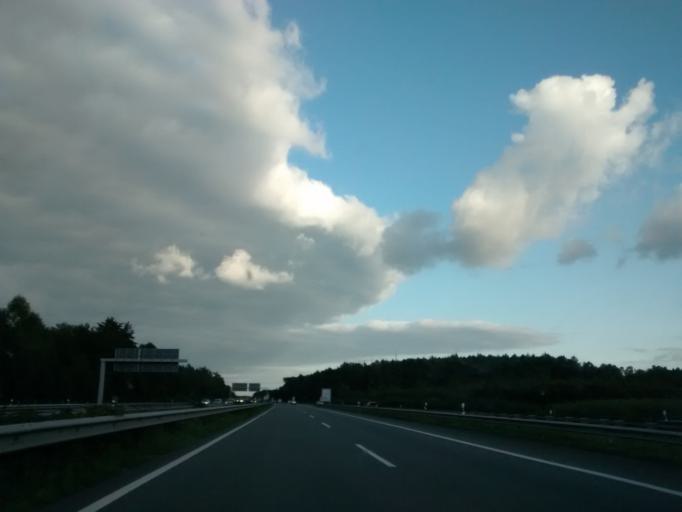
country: DE
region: Lower Saxony
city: Schuttorf
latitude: 52.3408
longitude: 7.2622
